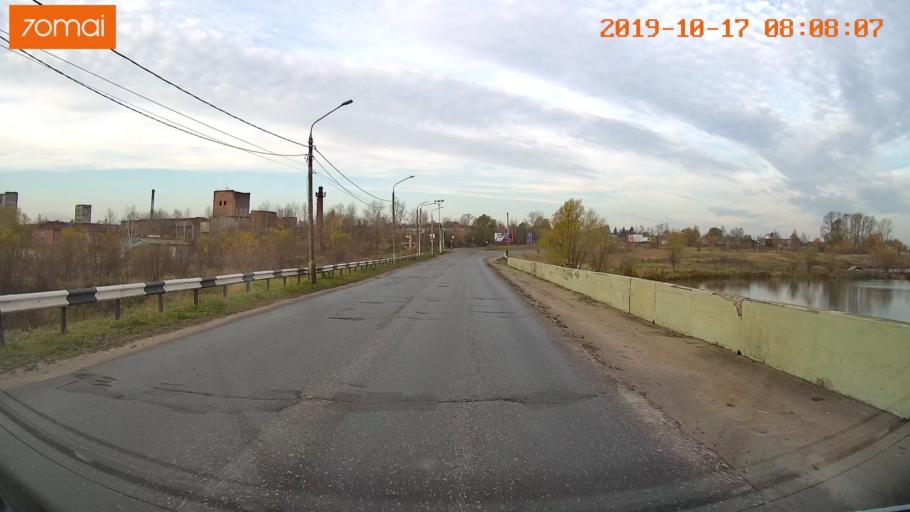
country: RU
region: Vladimir
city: Kol'chugino
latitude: 56.3144
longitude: 39.3925
